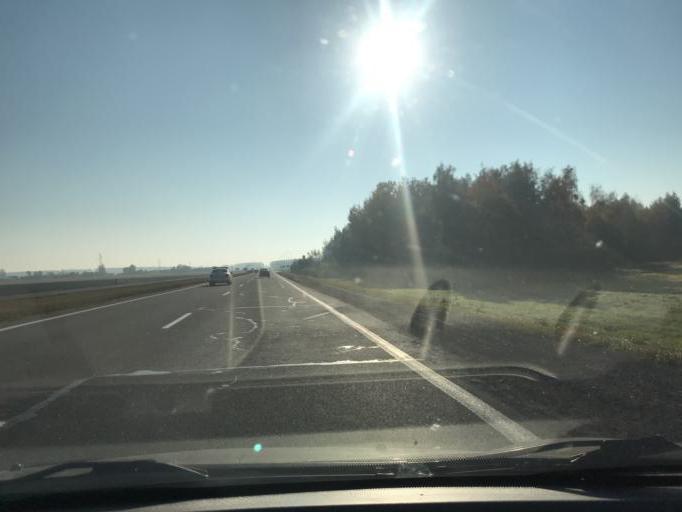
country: BY
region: Minsk
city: Dukora
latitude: 53.6365
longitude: 28.0077
